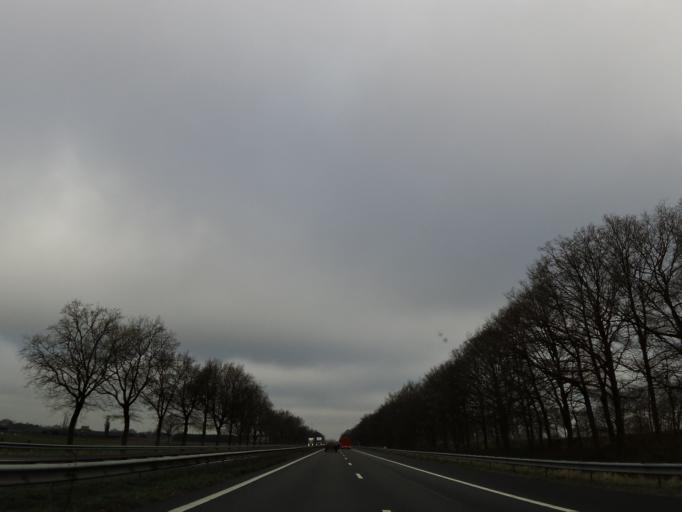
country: NL
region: Limburg
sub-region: Gemeente Leudal
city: Kelpen-Oler
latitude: 51.1975
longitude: 5.8318
